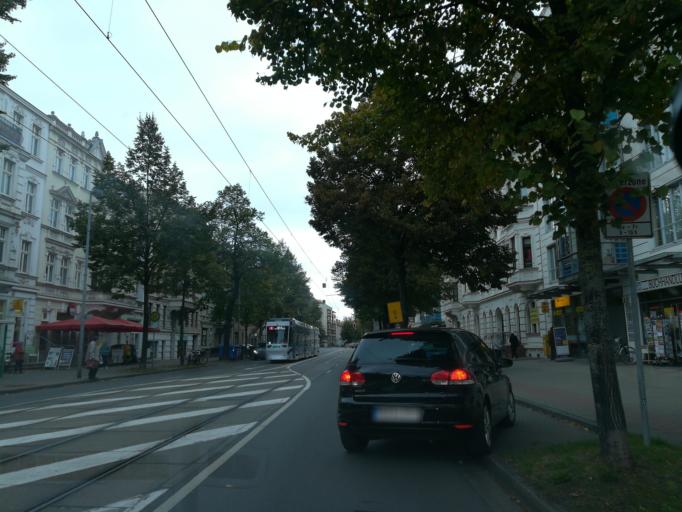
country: DE
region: Saxony-Anhalt
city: Magdeburg
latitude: 52.1340
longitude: 11.6183
